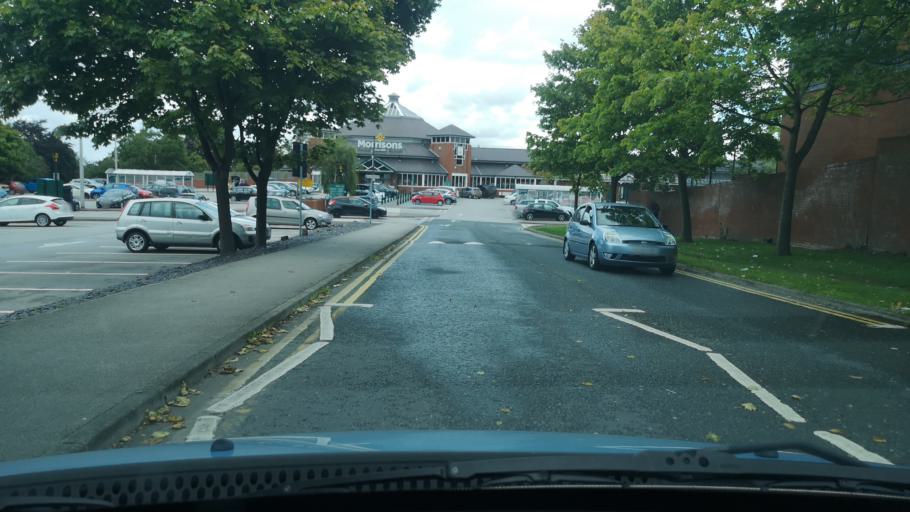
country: GB
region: England
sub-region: City and Borough of Wakefield
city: Pontefract
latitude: 53.6932
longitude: -1.3128
